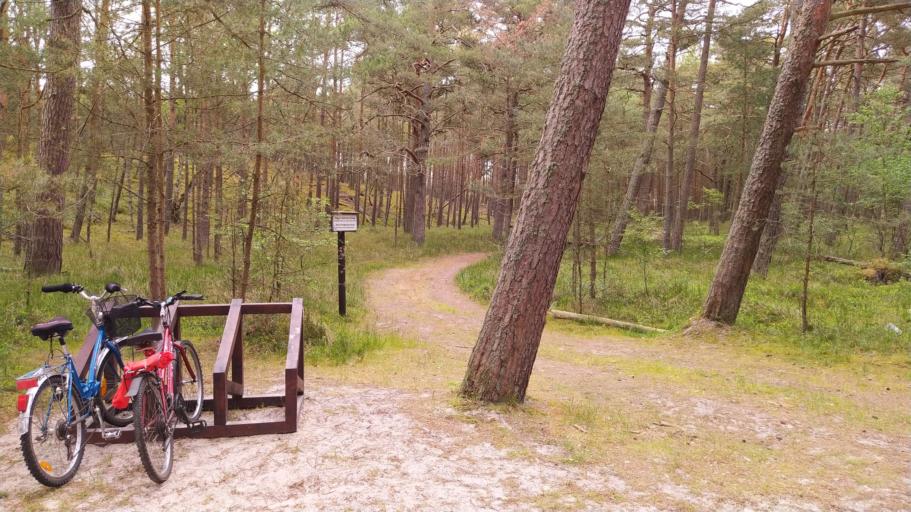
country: PL
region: Pomeranian Voivodeship
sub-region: Powiat slupski
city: Smoldzino
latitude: 54.6951
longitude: 17.1444
